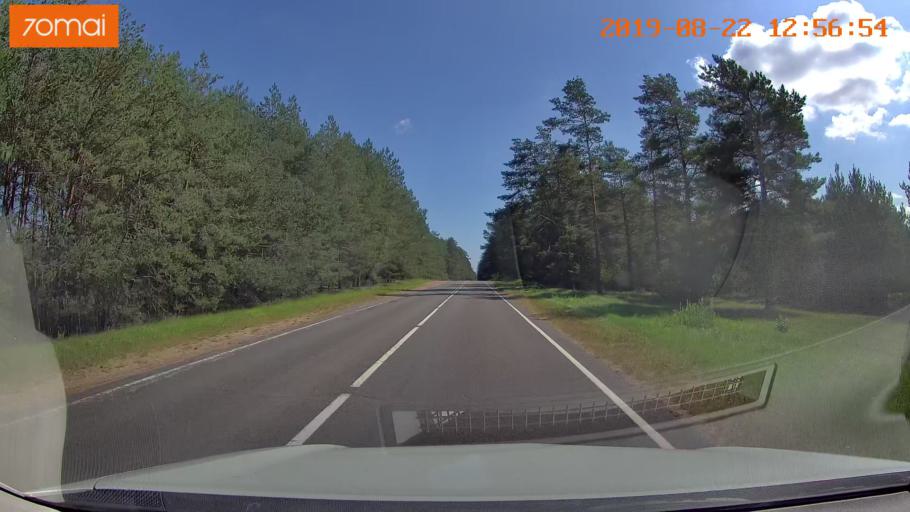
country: BY
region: Minsk
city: Prawdzinski
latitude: 53.4312
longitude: 27.7385
